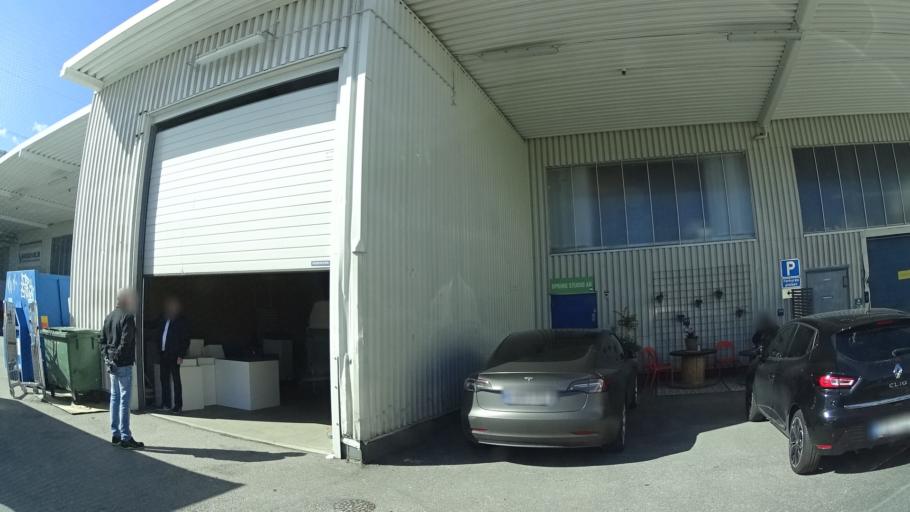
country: SE
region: Stockholm
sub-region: Huddinge Kommun
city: Segeltorp
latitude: 59.2845
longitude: 17.9288
